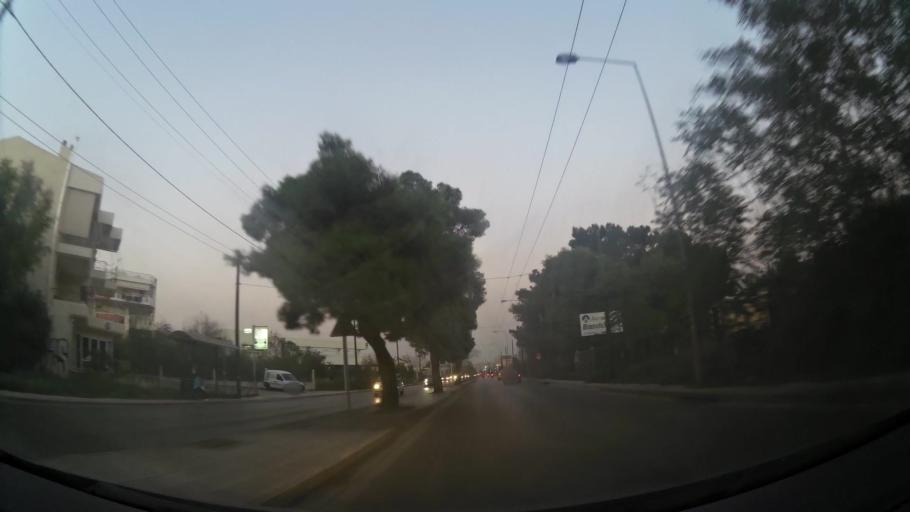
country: GR
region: Attica
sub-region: Nomarchia Athinas
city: Khalandrion
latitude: 38.0208
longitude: 23.8162
